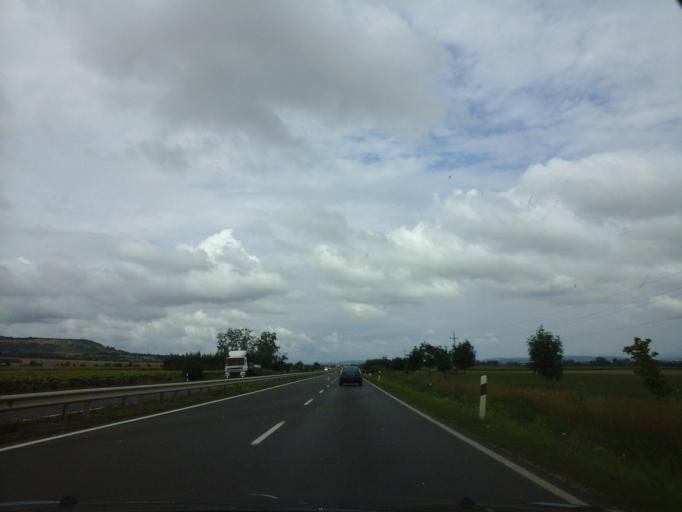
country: HU
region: Borsod-Abauj-Zemplen
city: Sajobabony
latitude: 48.1912
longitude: 20.7513
